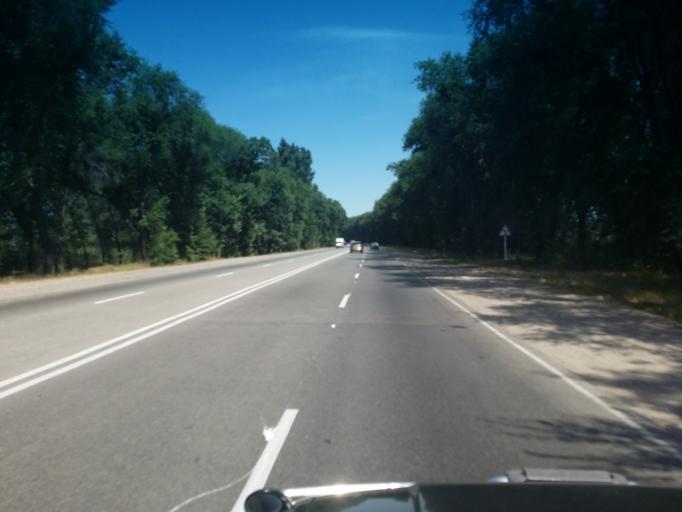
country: KZ
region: Almaty Oblysy
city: Talghar
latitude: 43.4068
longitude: 77.3053
